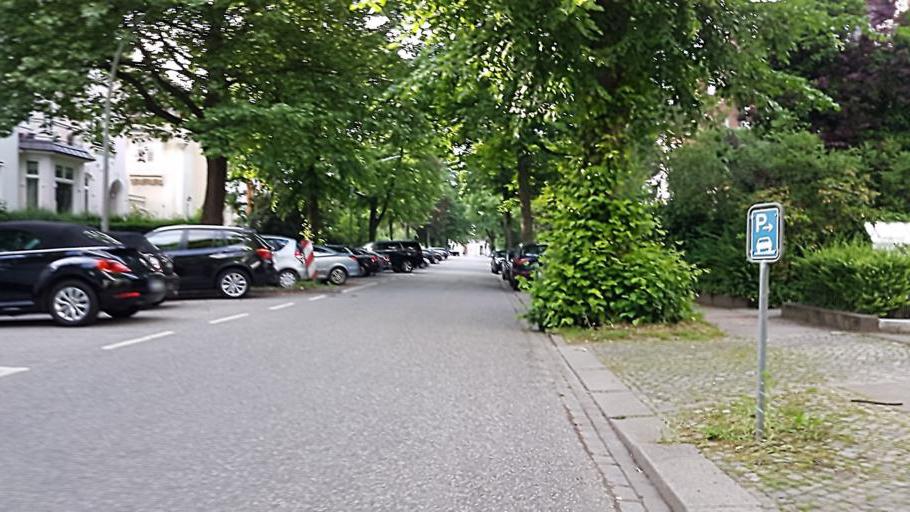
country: DE
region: Hamburg
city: Winterhude
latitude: 53.5834
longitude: 10.0004
